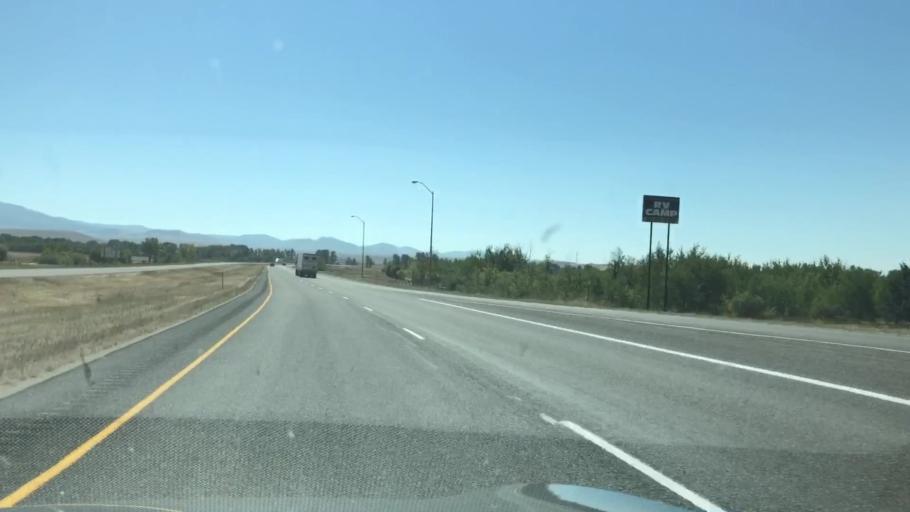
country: US
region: Montana
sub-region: Powell County
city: Deer Lodge
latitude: 46.4099
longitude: -112.7245
